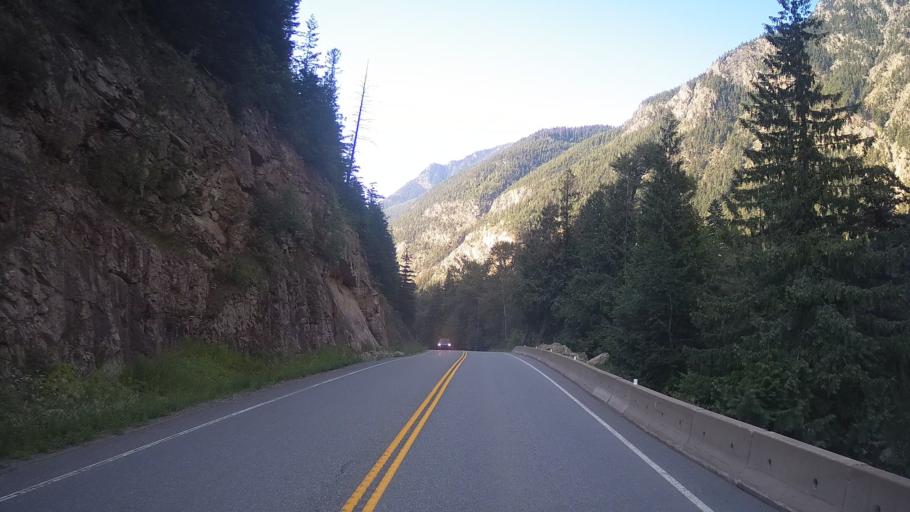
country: CA
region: British Columbia
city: Lillooet
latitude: 50.6227
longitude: -122.1019
